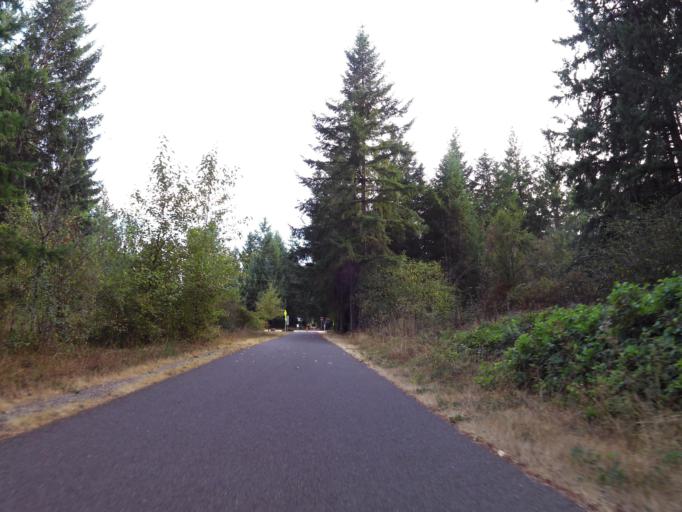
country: US
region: Washington
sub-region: Thurston County
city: Lacey
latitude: 46.9592
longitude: -122.8119
